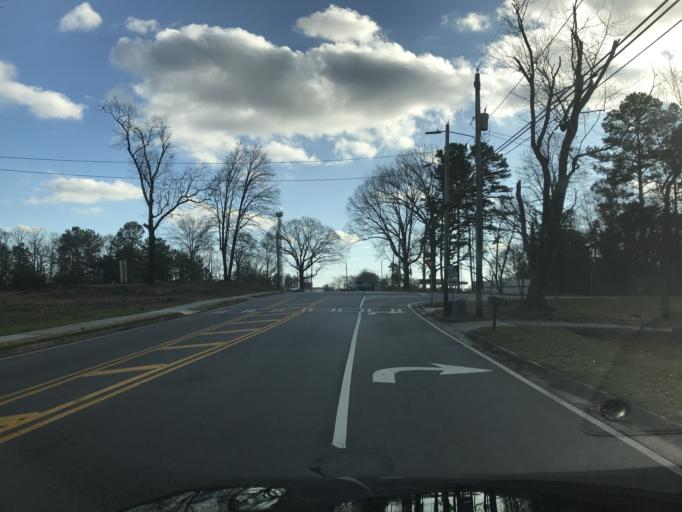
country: US
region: Georgia
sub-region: Fulton County
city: College Park
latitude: 33.6299
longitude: -84.4727
